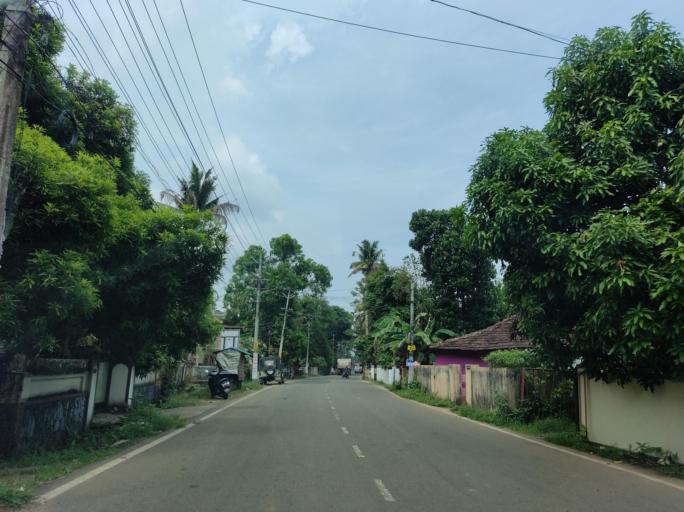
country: IN
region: Kerala
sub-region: Kottayam
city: Kottayam
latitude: 9.5828
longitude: 76.5051
